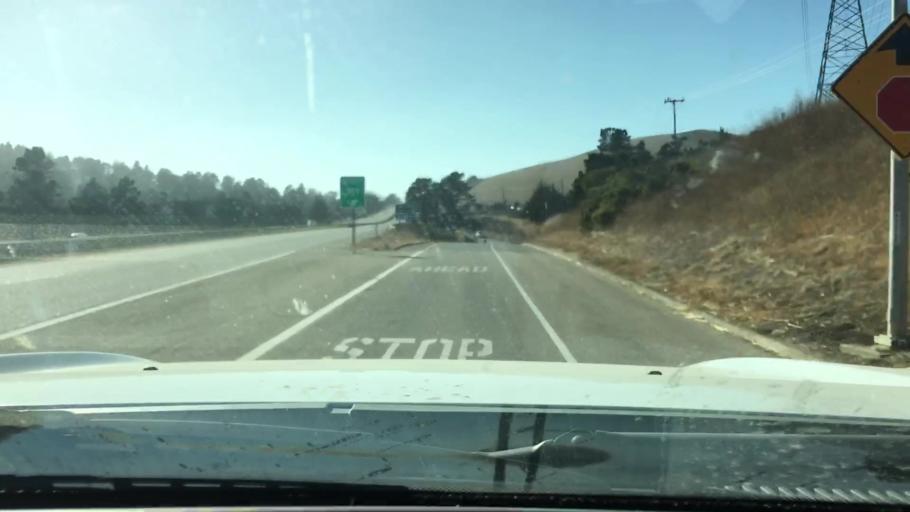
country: US
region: California
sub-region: San Luis Obispo County
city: Morro Bay
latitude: 35.3637
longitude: -120.8189
